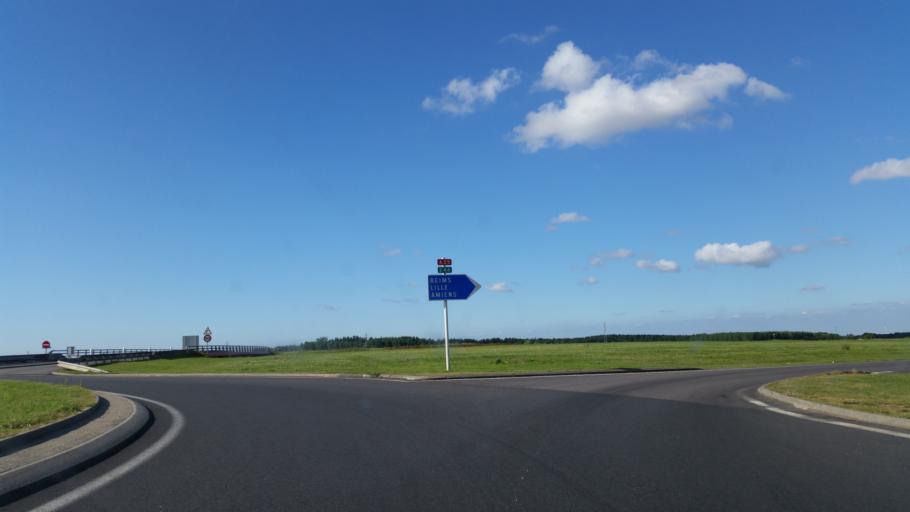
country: FR
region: Picardie
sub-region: Departement de la Somme
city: Poix-de-Picardie
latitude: 49.8092
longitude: 1.9729
